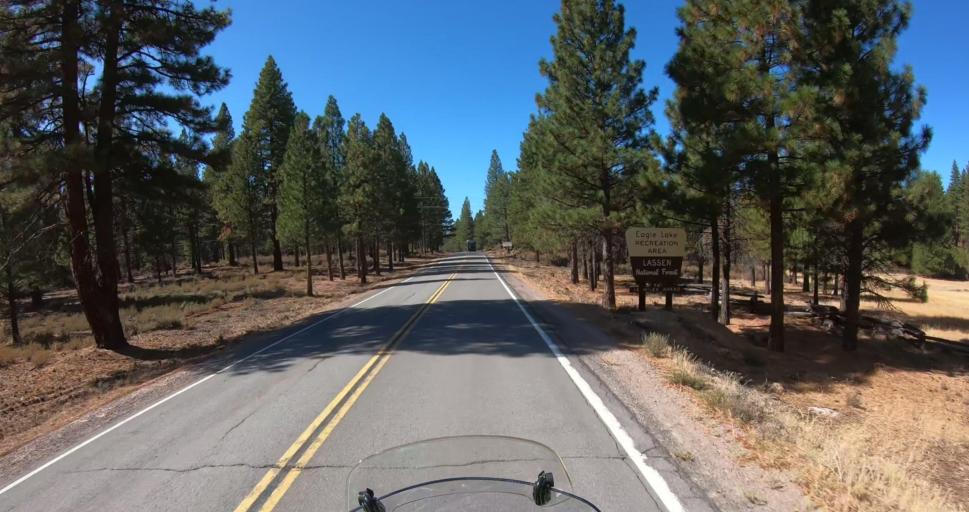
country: US
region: California
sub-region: Lassen County
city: Susanville
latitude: 40.4213
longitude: -120.7075
